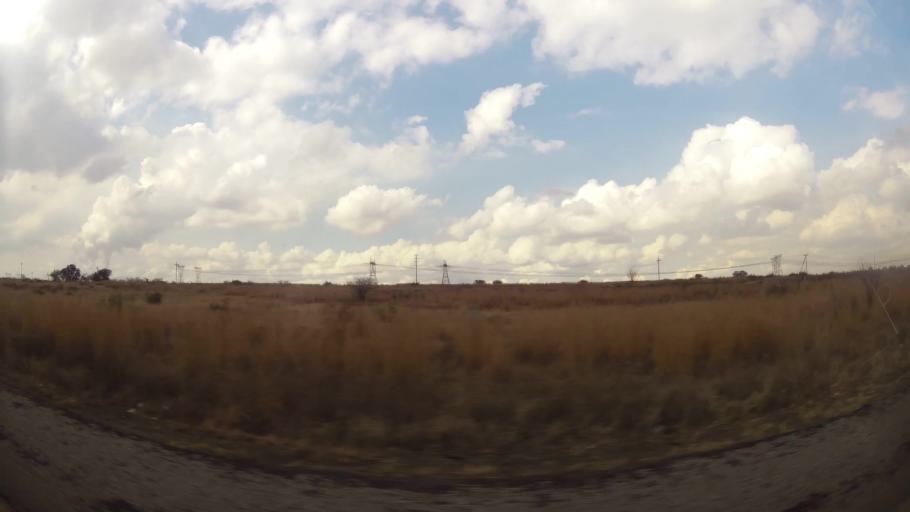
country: ZA
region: Orange Free State
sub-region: Fezile Dabi District Municipality
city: Sasolburg
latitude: -26.7925
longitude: 27.9169
